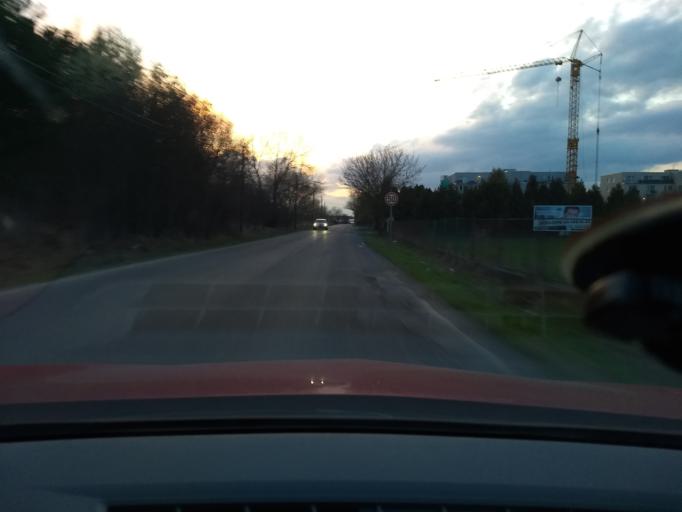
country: CZ
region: Central Bohemia
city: Hostivice
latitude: 50.0582
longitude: 14.2476
